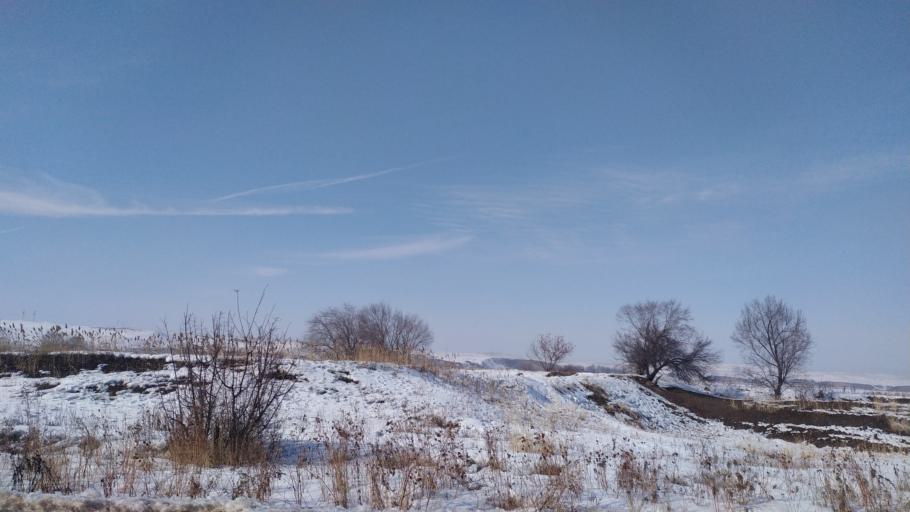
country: KZ
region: Almaty Oblysy
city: Burunday
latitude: 43.2360
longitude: 76.4118
